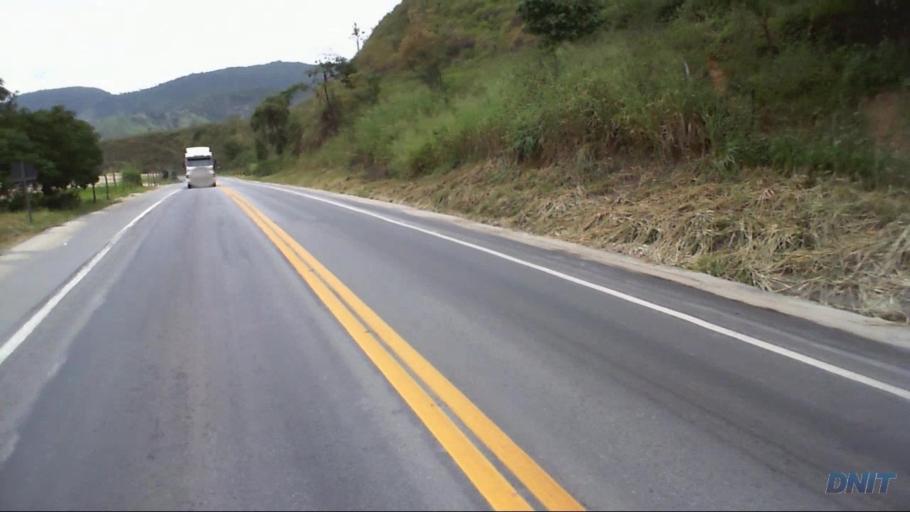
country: BR
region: Minas Gerais
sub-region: Timoteo
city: Timoteo
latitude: -19.6187
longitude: -42.7871
